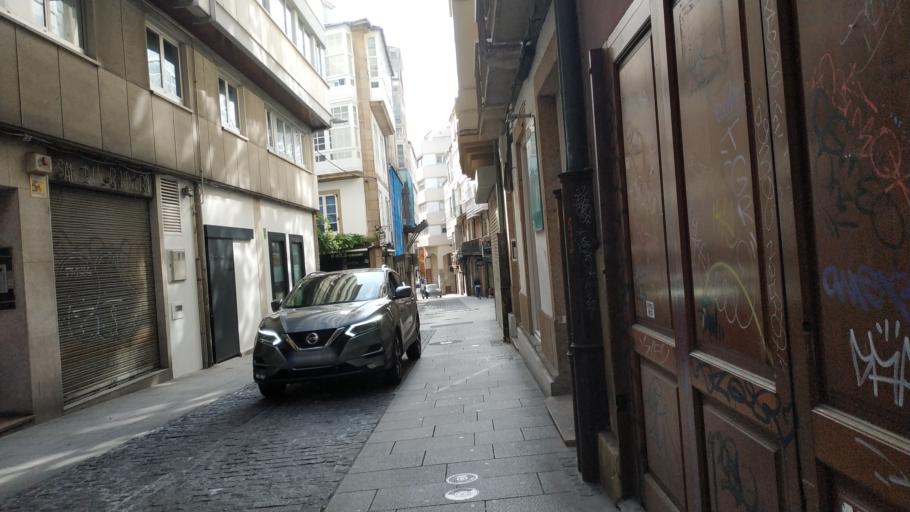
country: ES
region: Galicia
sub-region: Provincia da Coruna
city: A Coruna
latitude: 43.3720
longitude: -8.3997
